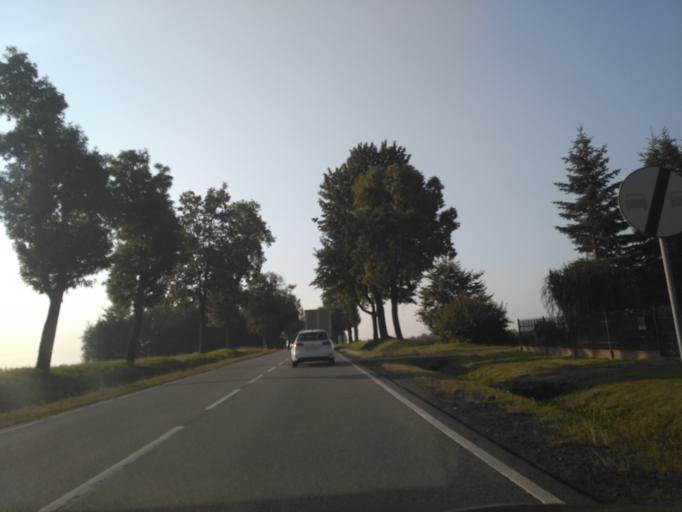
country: PL
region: Lublin Voivodeship
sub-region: Powiat krasnicki
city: Szastarka
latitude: 50.8423
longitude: 22.2967
